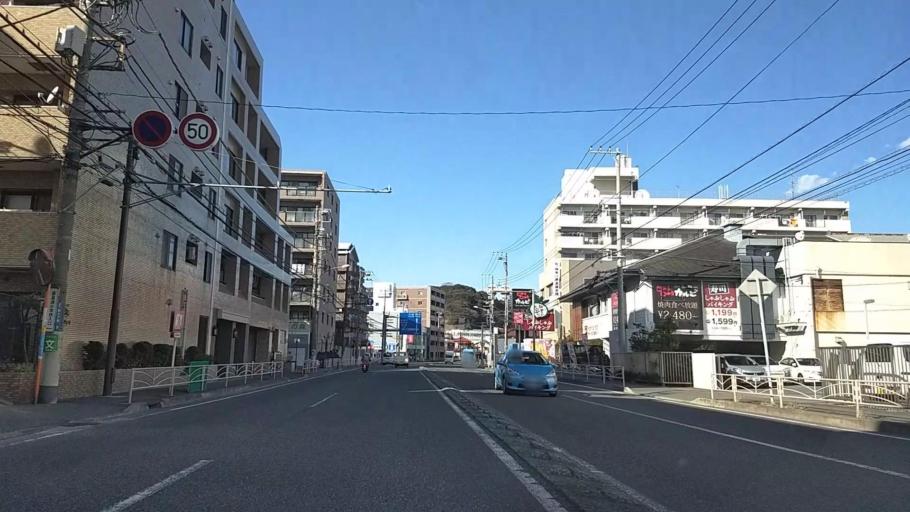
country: JP
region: Kanagawa
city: Yokohama
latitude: 35.3914
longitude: 139.6149
